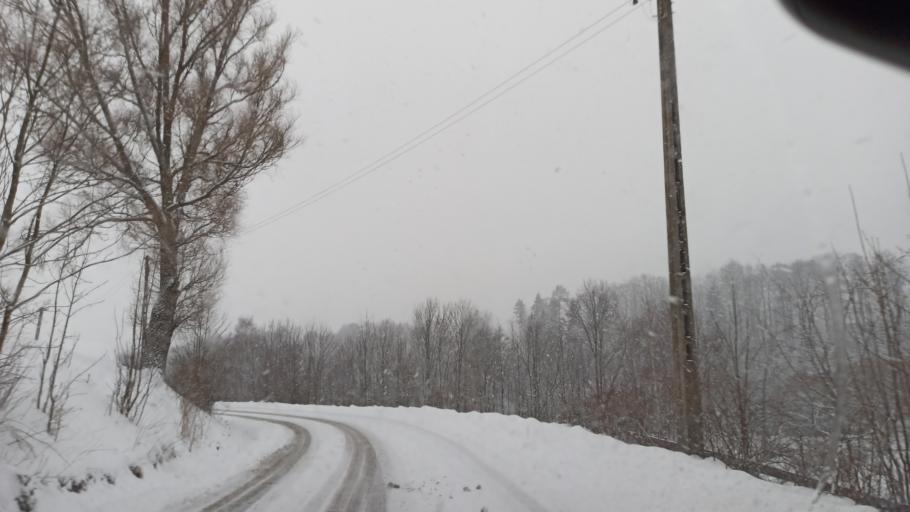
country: PL
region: Lower Silesian Voivodeship
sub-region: Powiat klodzki
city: Ludwikowice Klodzkie
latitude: 50.6518
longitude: 16.4729
